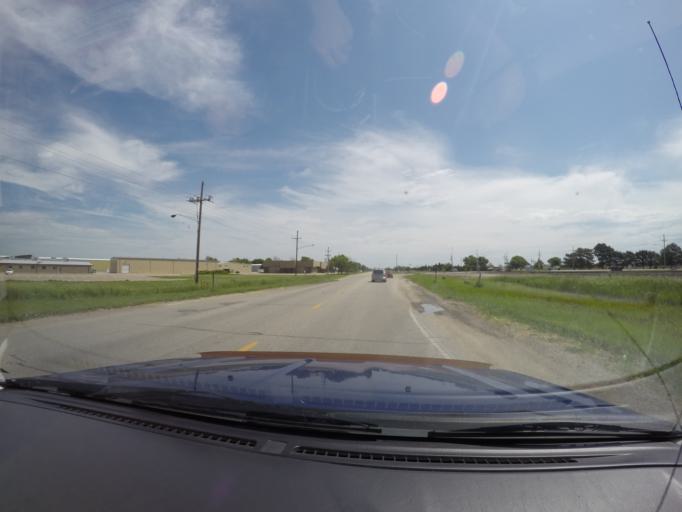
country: US
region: Nebraska
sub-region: Hall County
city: Grand Island
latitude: 40.9023
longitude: -98.3969
